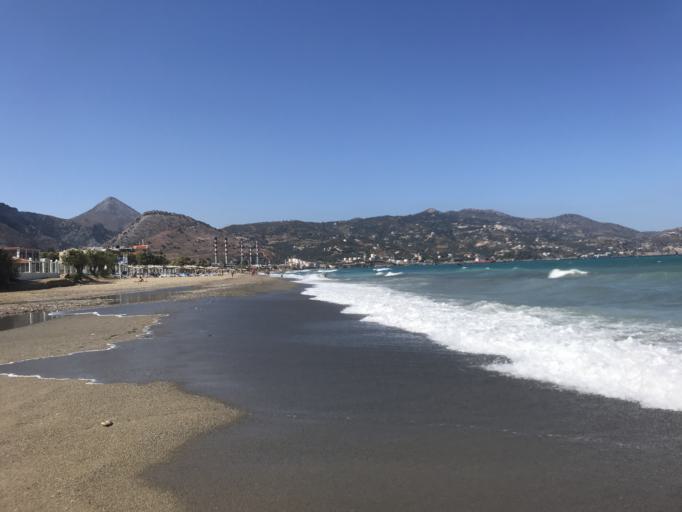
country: GR
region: Crete
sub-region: Nomos Irakleiou
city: Gazi
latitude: 35.3391
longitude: 25.0656
